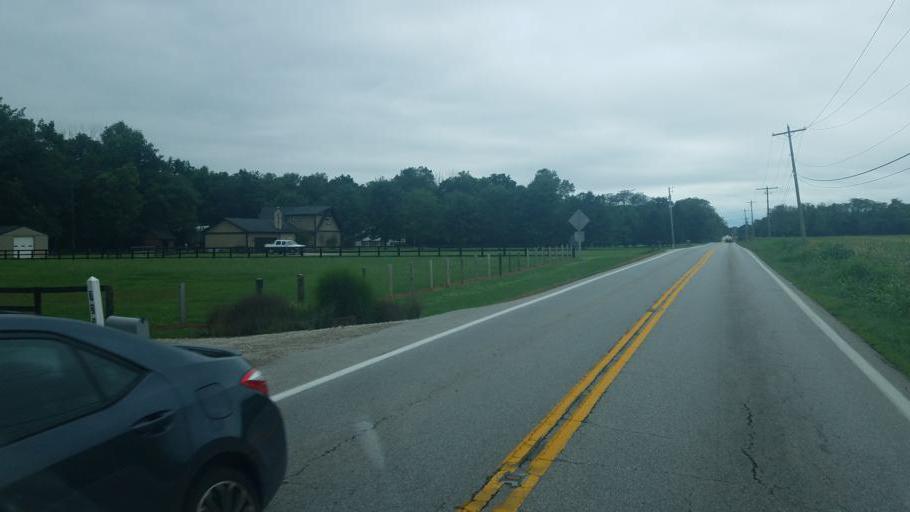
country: US
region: Ohio
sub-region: Pickaway County
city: Commercial Point
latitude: 39.8240
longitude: -83.0192
